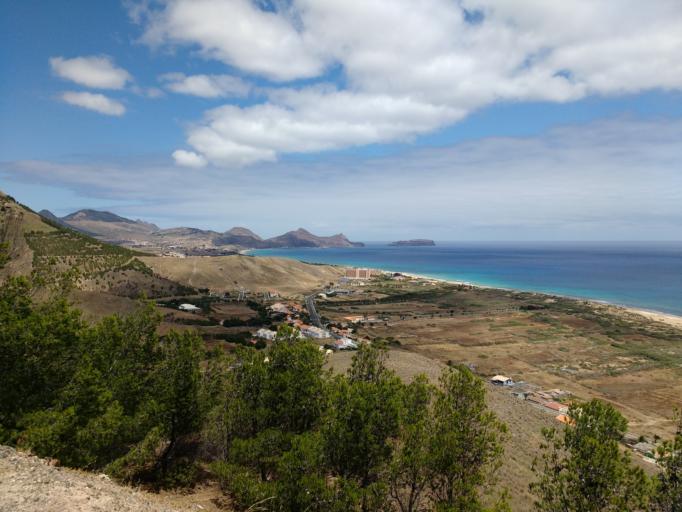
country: PT
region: Madeira
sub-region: Porto Santo
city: Vila de Porto Santo
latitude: 33.0321
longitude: -16.3791
